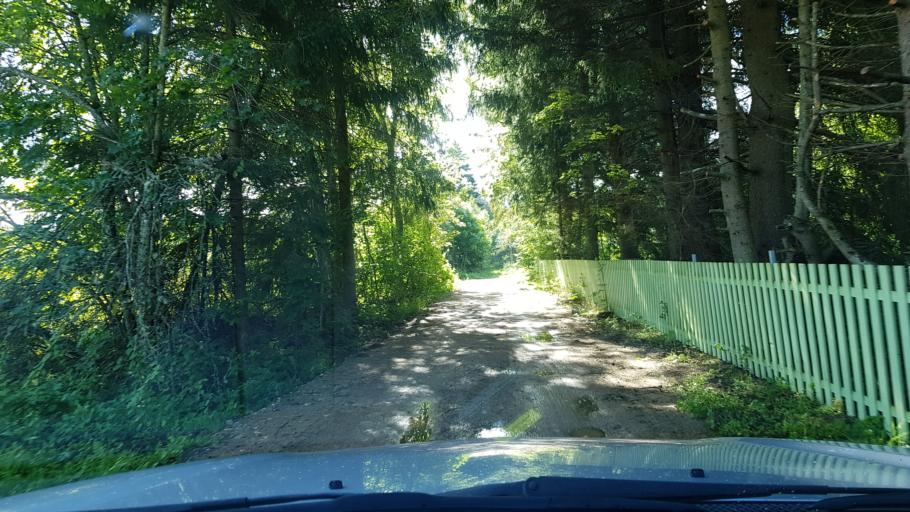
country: EE
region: Harju
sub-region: Raasiku vald
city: Arukula
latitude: 59.2555
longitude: 25.0999
